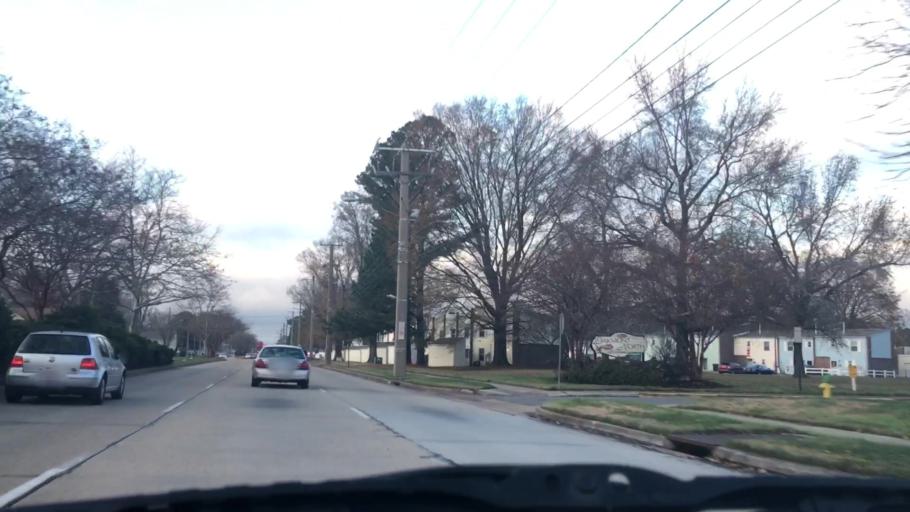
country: US
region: Virginia
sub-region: City of Norfolk
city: Norfolk
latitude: 36.9095
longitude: -76.2405
